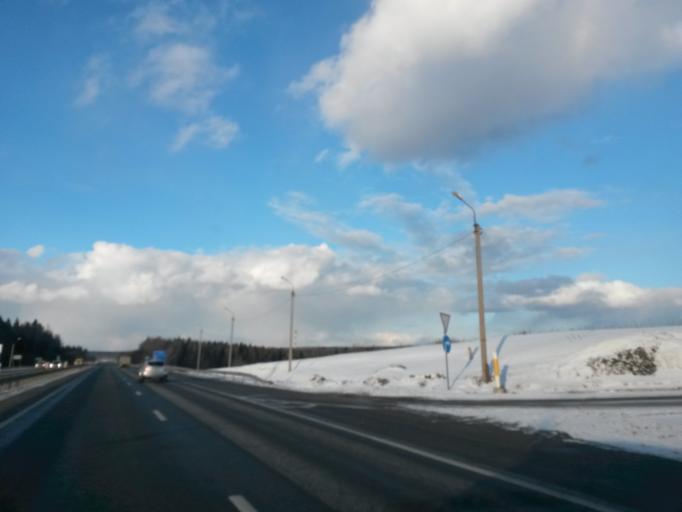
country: RU
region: Moskovskaya
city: Sergiyev Posad
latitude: 56.2493
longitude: 38.1625
